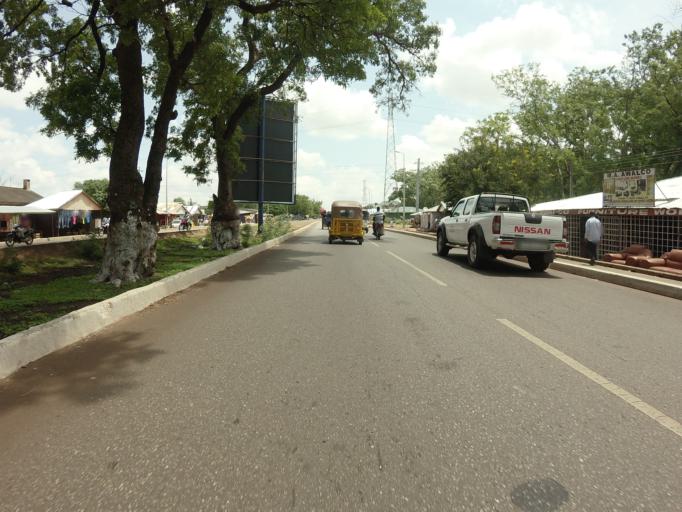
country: GH
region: Northern
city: Tamale
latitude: 9.4044
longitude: -0.8577
